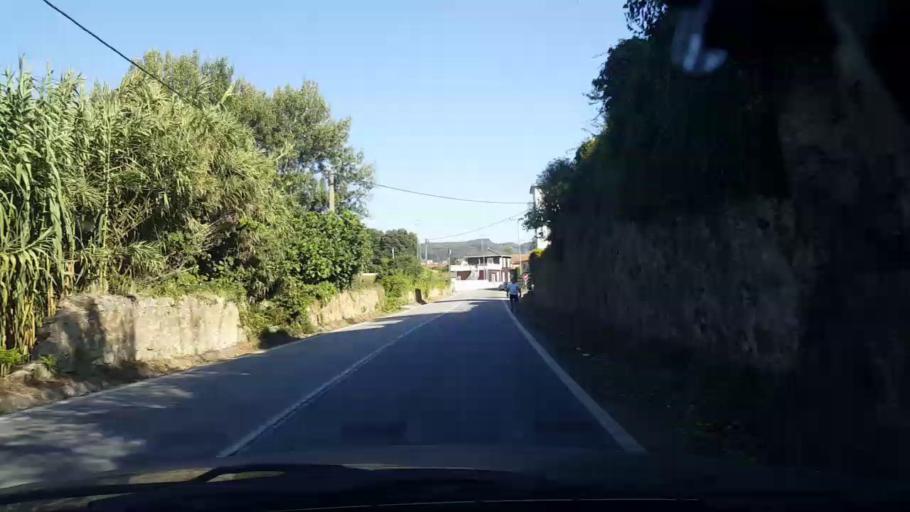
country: PT
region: Porto
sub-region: Vila do Conde
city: Arvore
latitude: 41.3337
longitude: -8.6668
